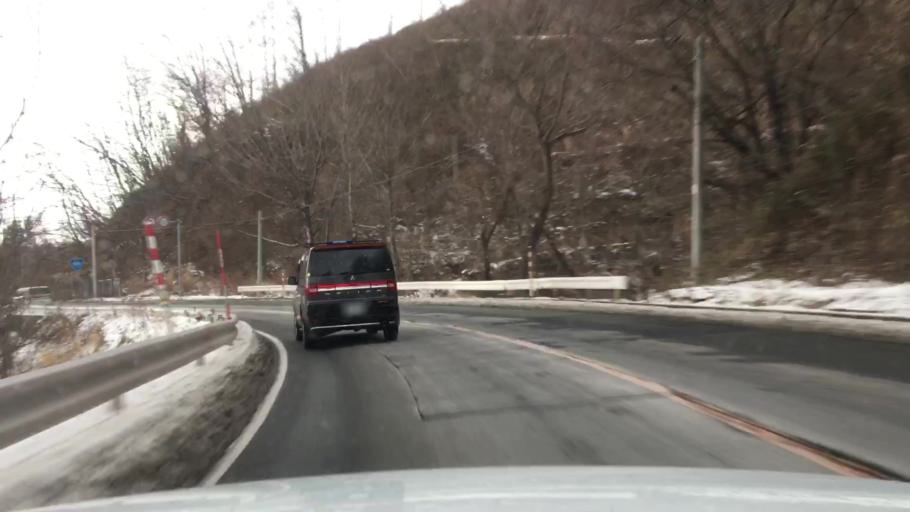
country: JP
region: Iwate
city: Morioka-shi
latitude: 39.6601
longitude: 141.3369
